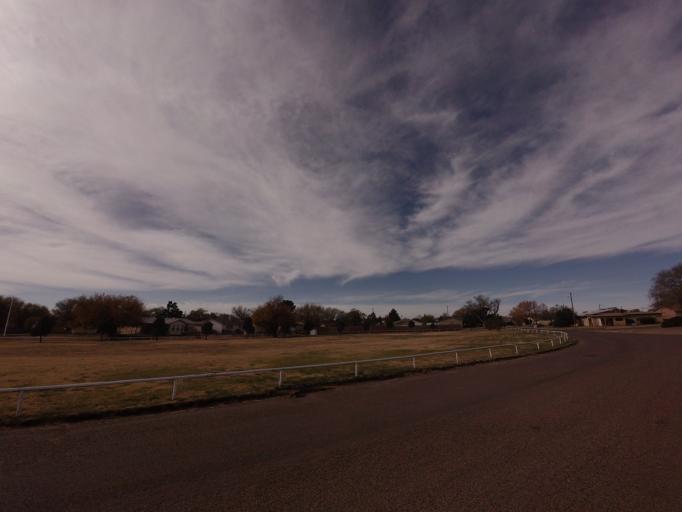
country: US
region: New Mexico
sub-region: Curry County
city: Clovis
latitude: 34.4129
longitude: -103.1932
